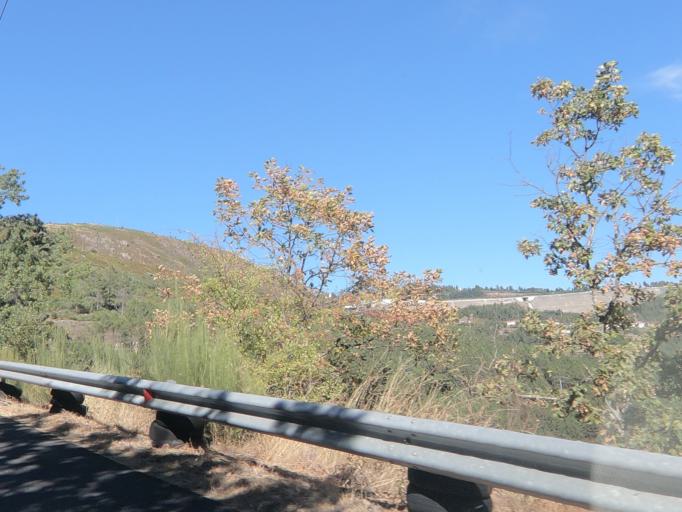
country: PT
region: Vila Real
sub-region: Santa Marta de Penaguiao
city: Santa Marta de Penaguiao
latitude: 41.2677
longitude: -7.8739
